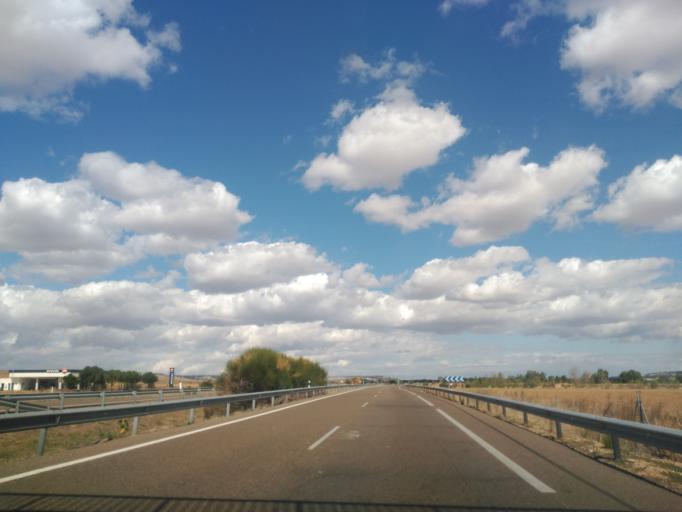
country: ES
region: Castille and Leon
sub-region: Provincia de Palencia
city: Torquemada
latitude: 42.0147
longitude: -4.3475
